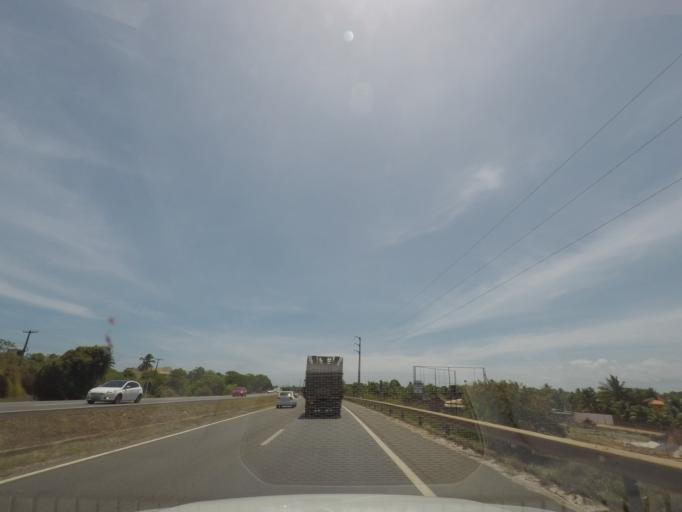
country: BR
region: Bahia
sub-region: Camacari
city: Camacari
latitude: -12.6501
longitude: -38.0830
